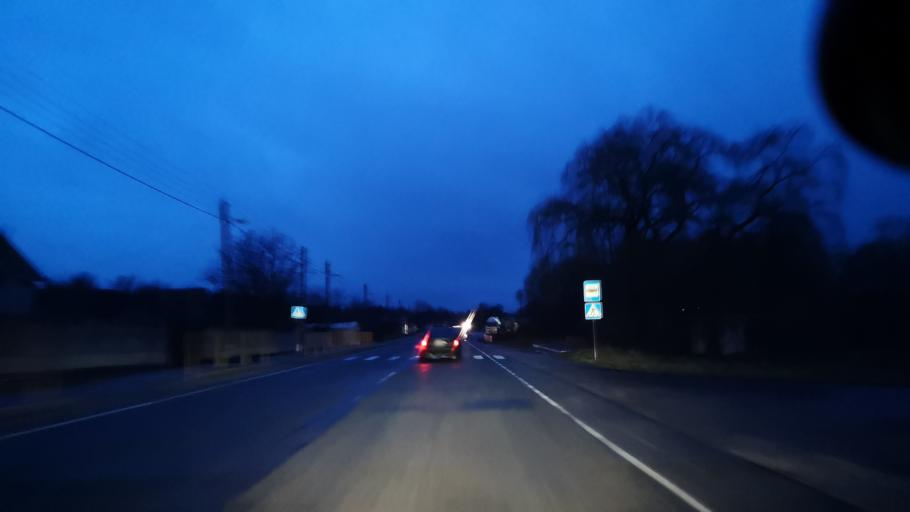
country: MD
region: Orhei
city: Orhei
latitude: 47.4281
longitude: 28.8022
